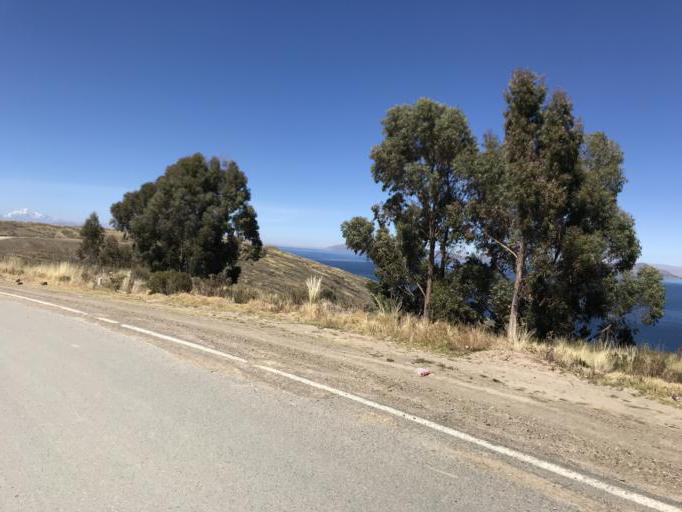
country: BO
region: La Paz
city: San Pablo
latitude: -16.1980
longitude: -68.8259
